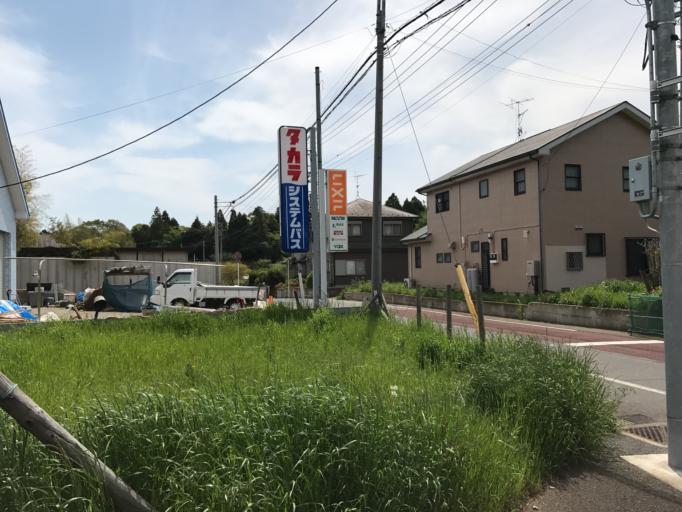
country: JP
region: Chiba
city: Yotsukaido
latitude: 35.5849
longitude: 140.1988
